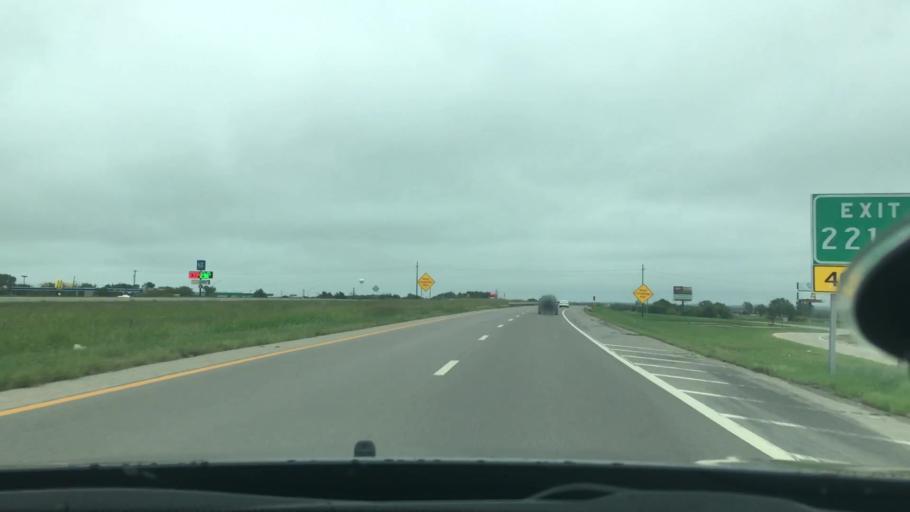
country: US
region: Oklahoma
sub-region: Okfuskee County
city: Okemah
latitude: 35.4220
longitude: -96.3030
